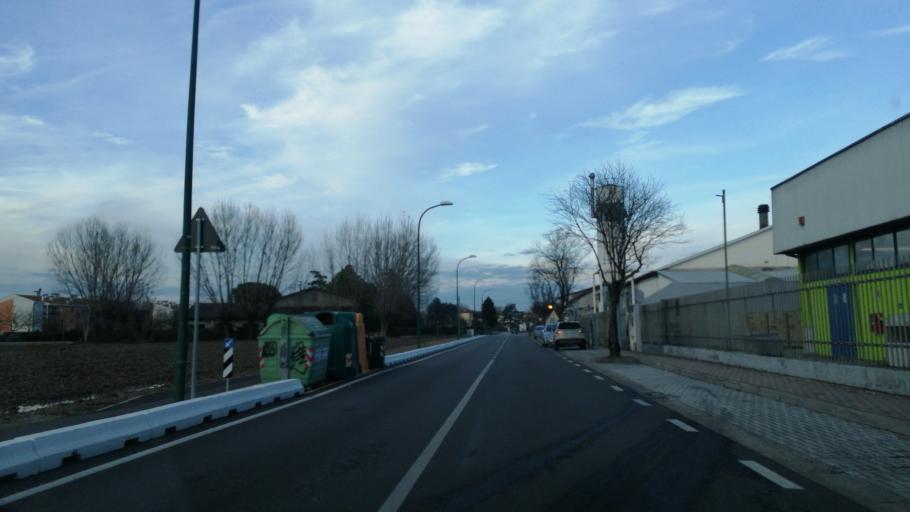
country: IT
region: Veneto
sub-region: Provincia di Venezia
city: Zelarino
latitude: 45.4916
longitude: 12.2107
